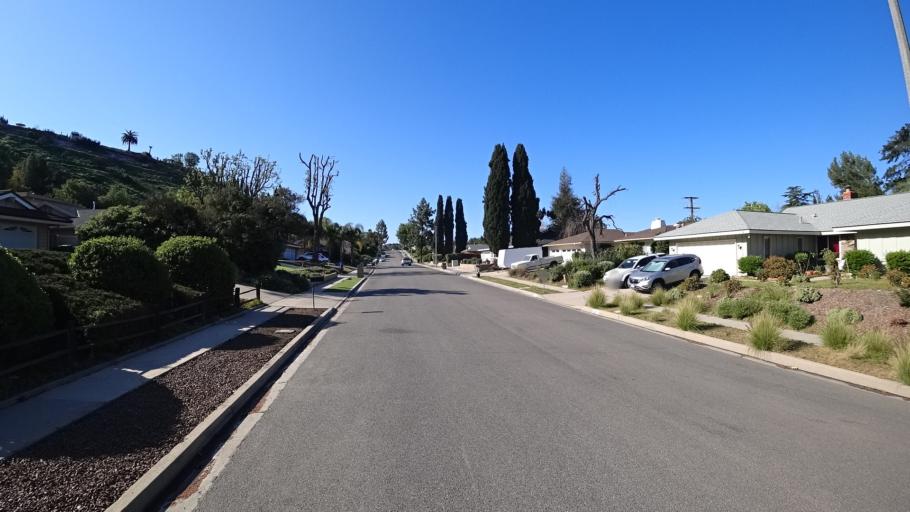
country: US
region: California
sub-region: Ventura County
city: Thousand Oaks
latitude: 34.1992
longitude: -118.8417
